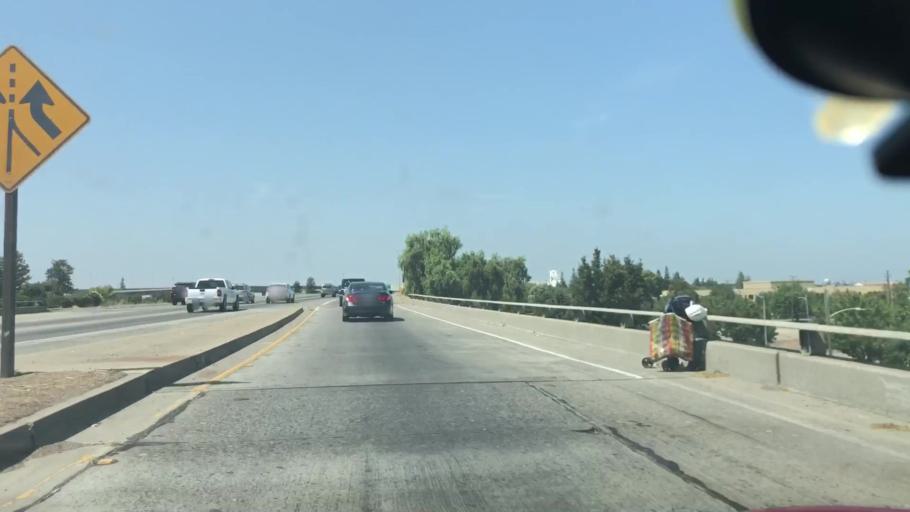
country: US
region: California
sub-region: San Joaquin County
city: Stockton
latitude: 37.9500
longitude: -121.2929
